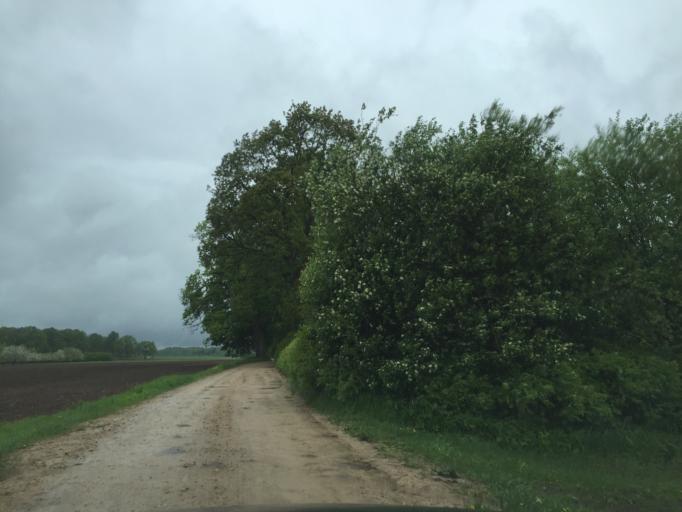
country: LV
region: Ogre
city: Jumprava
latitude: 56.6657
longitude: 24.9999
